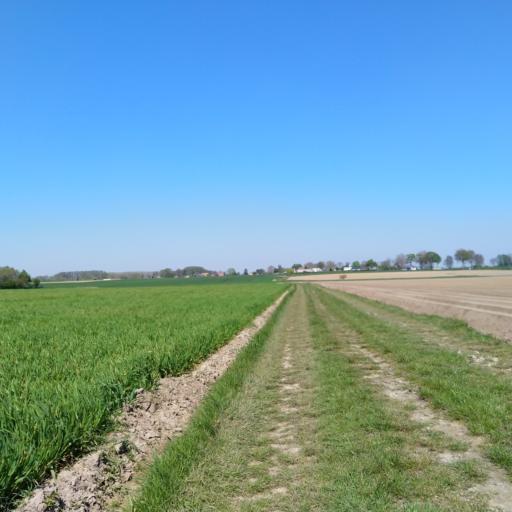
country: BE
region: Wallonia
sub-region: Province du Hainaut
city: Jurbise
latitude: 50.5397
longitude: 3.9035
